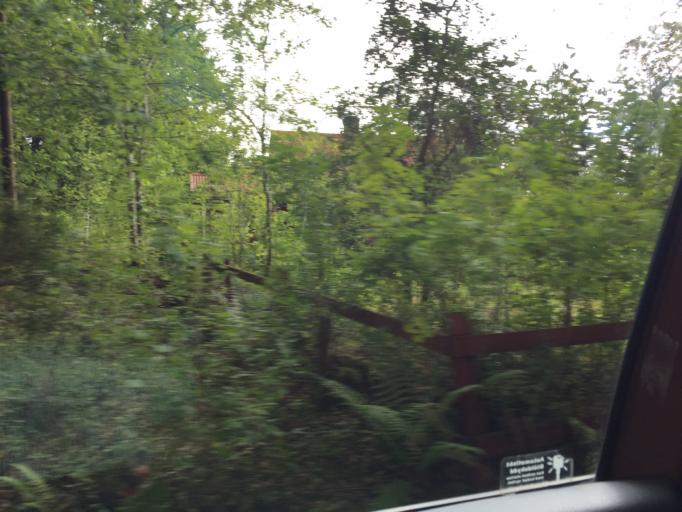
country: SE
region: Kalmar
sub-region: Vasterviks Kommun
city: Gamleby
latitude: 57.7859
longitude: 16.4256
